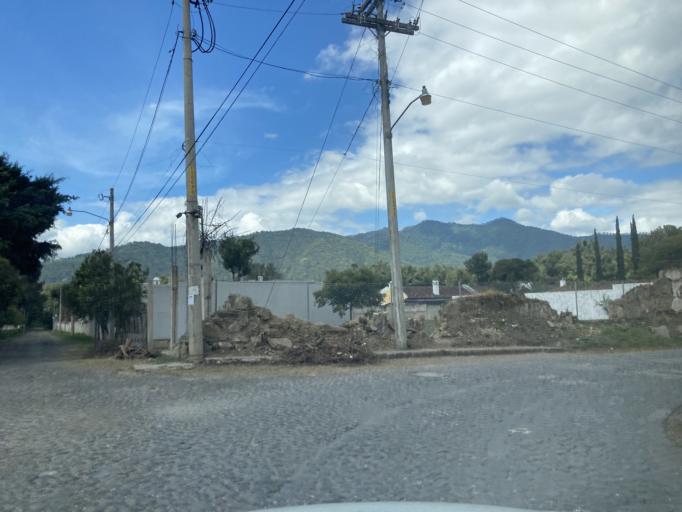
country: GT
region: Sacatepequez
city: Antigua Guatemala
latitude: 14.5485
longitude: -90.7342
